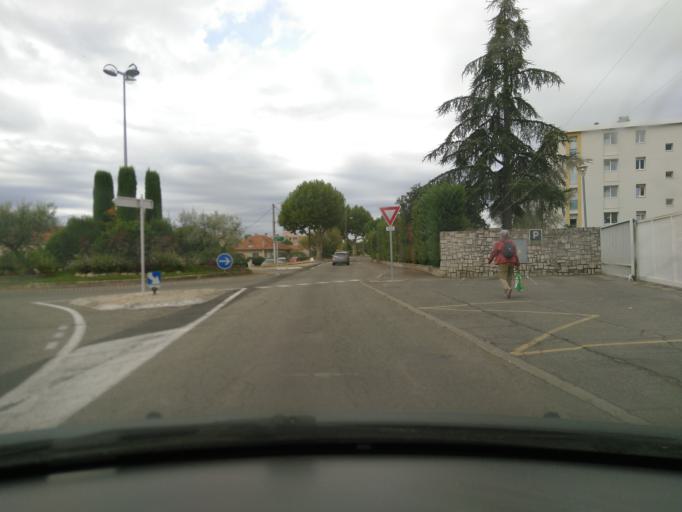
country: FR
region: Rhone-Alpes
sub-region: Departement de la Drome
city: Nyons
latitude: 44.3567
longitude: 5.1263
